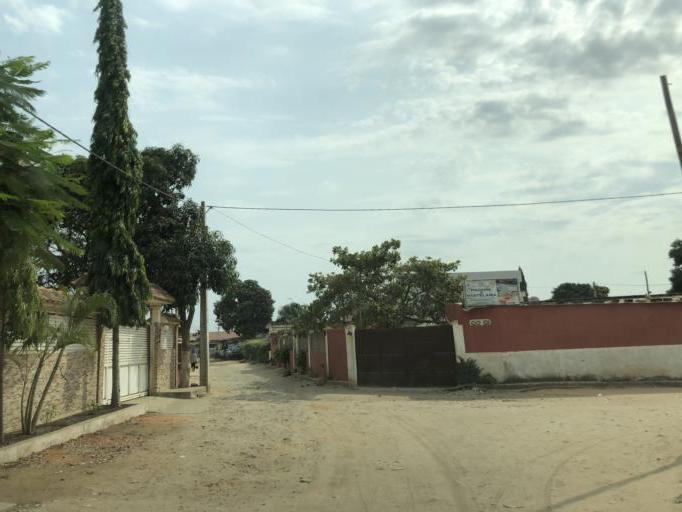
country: AO
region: Luanda
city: Luanda
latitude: -8.8949
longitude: 13.3547
